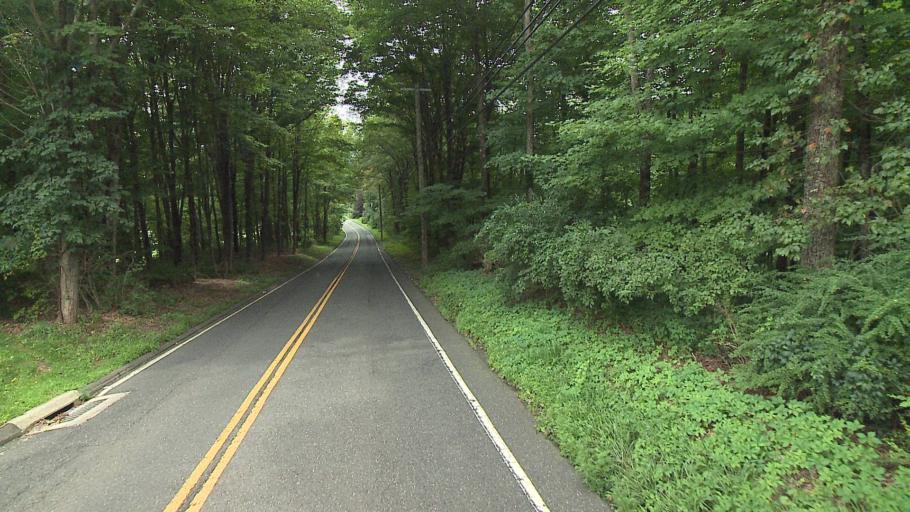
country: US
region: Connecticut
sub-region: Litchfield County
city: Woodbury
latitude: 41.5590
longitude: -73.2851
